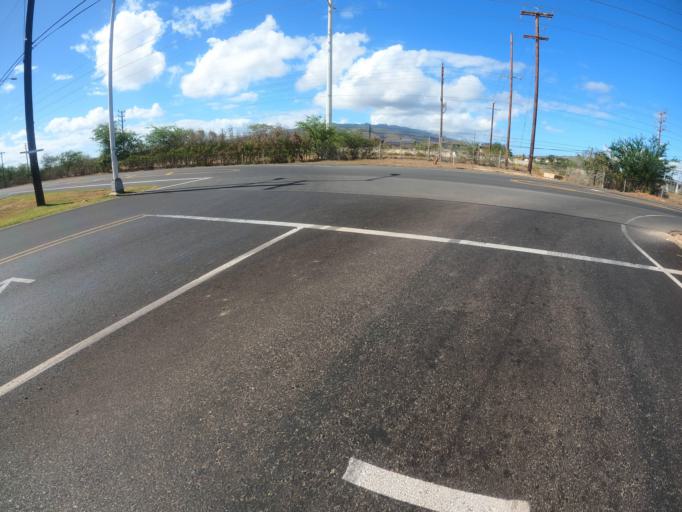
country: US
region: Hawaii
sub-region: Honolulu County
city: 'Ewa Villages
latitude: 21.3289
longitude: -158.0549
